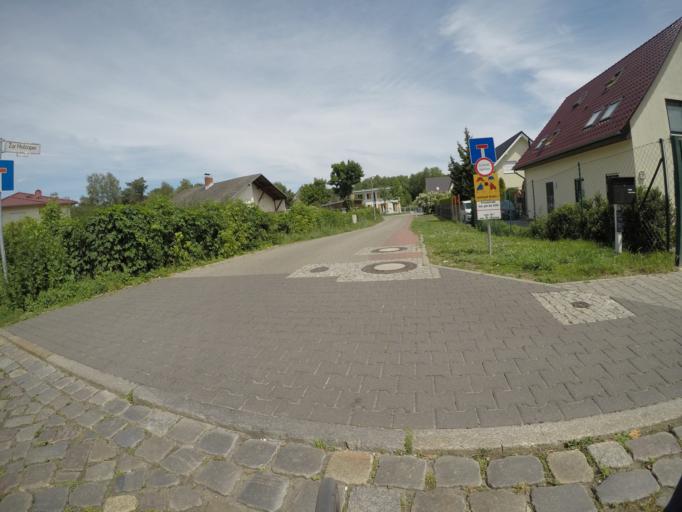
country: DE
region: Berlin
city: Adlershof
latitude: 52.4420
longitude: 13.5424
